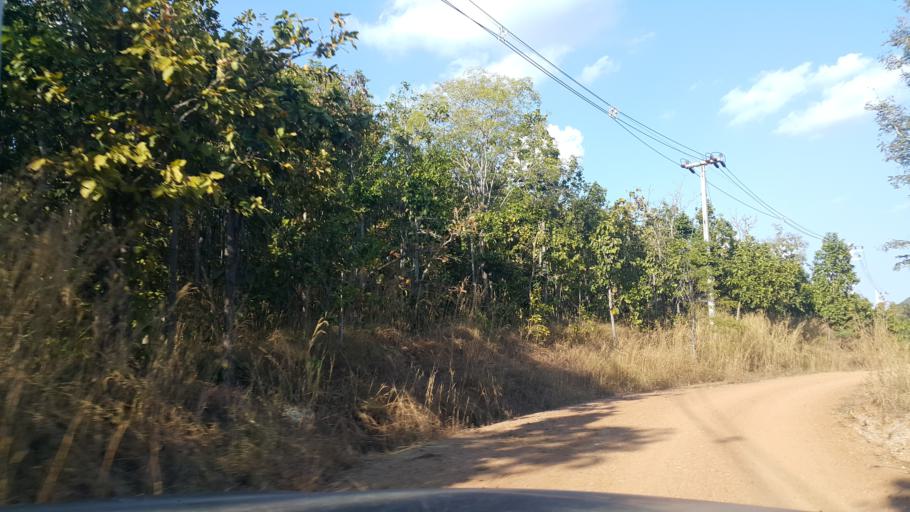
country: TH
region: Lamphun
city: Mae Tha
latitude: 18.5271
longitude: 99.1225
